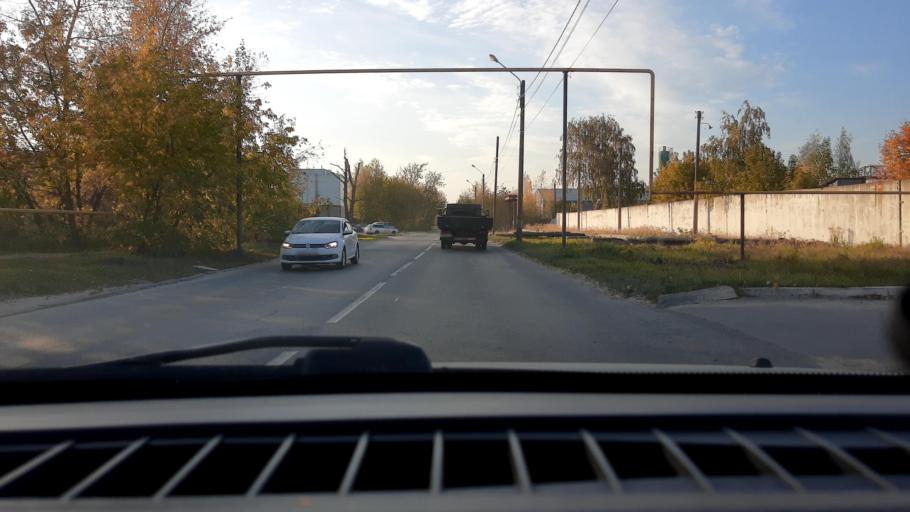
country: RU
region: Nizjnij Novgorod
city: Gorbatovka
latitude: 56.3486
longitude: 43.8143
